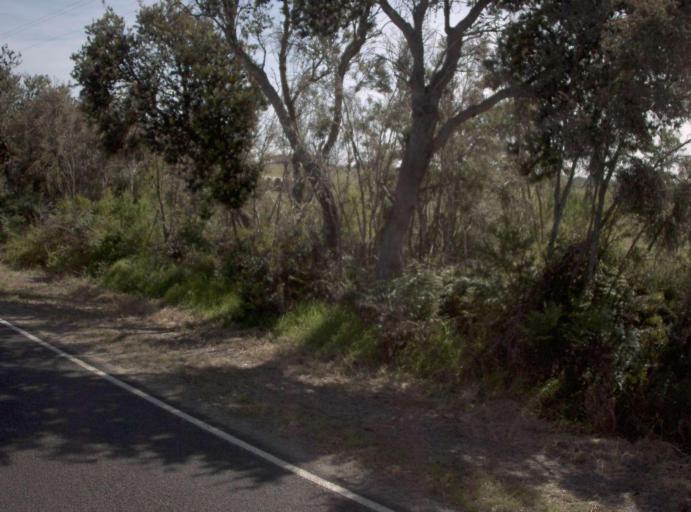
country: AU
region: Victoria
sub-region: Wellington
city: Sale
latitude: -38.3525
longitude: 147.1713
